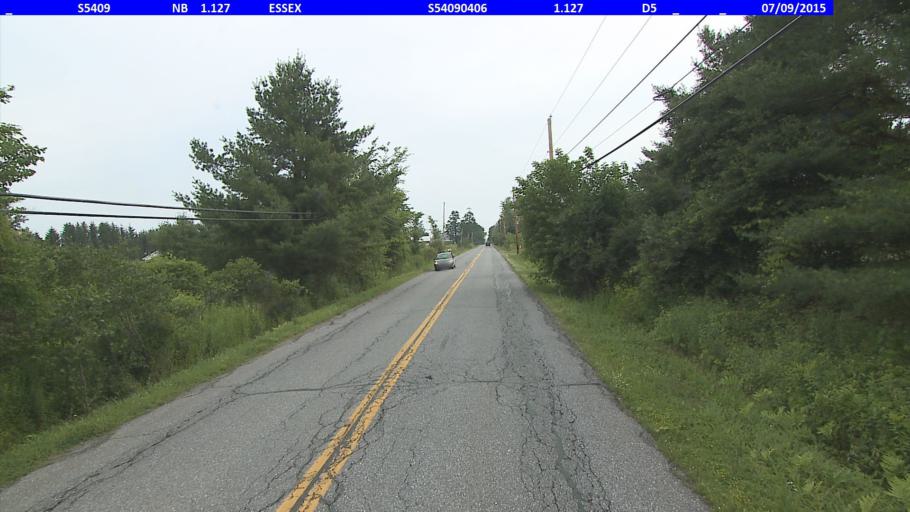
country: US
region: Vermont
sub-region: Chittenden County
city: Essex Junction
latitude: 44.5257
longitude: -73.0783
